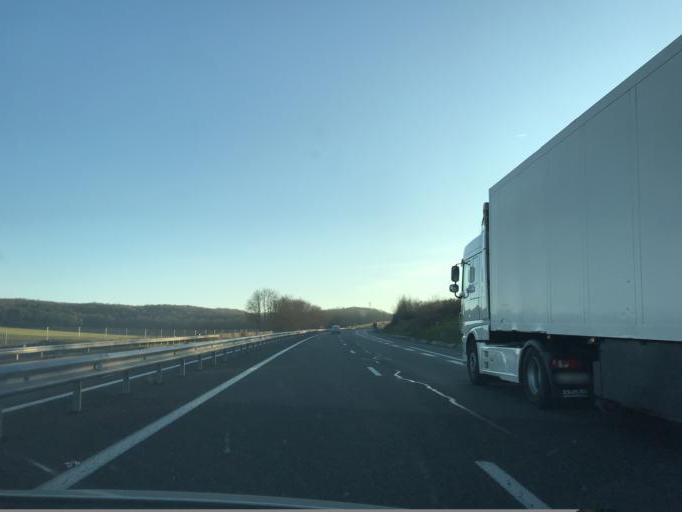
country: FR
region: Bourgogne
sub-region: Departement de l'Yonne
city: Saint-Martin-du-Tertre
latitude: 48.2189
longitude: 3.2360
